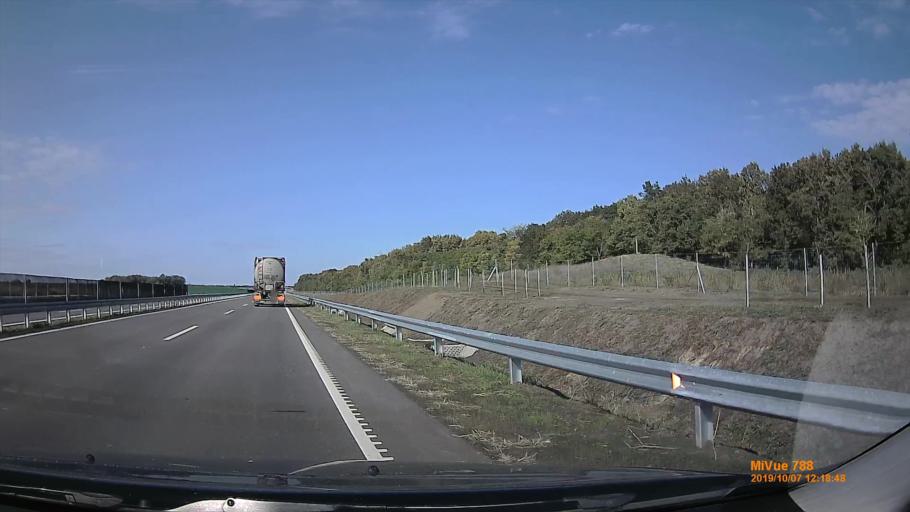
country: HU
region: Jasz-Nagykun-Szolnok
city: Kunszentmarton
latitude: 46.8421
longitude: 20.3354
